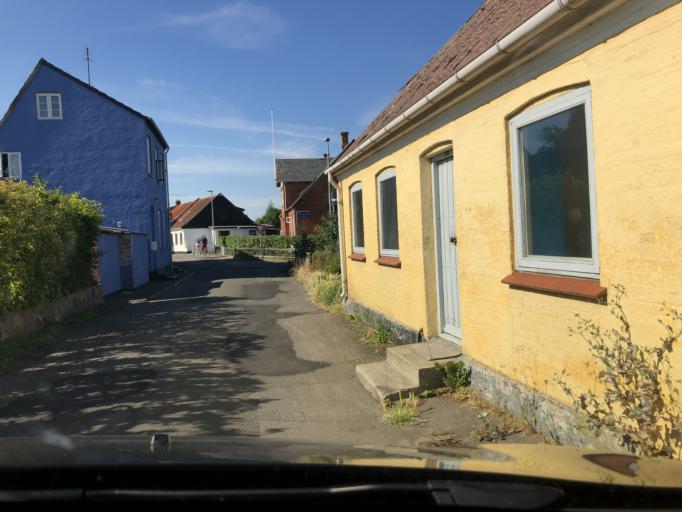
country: DK
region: South Denmark
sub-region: AEro Kommune
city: Marstal
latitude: 54.8576
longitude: 10.5158
